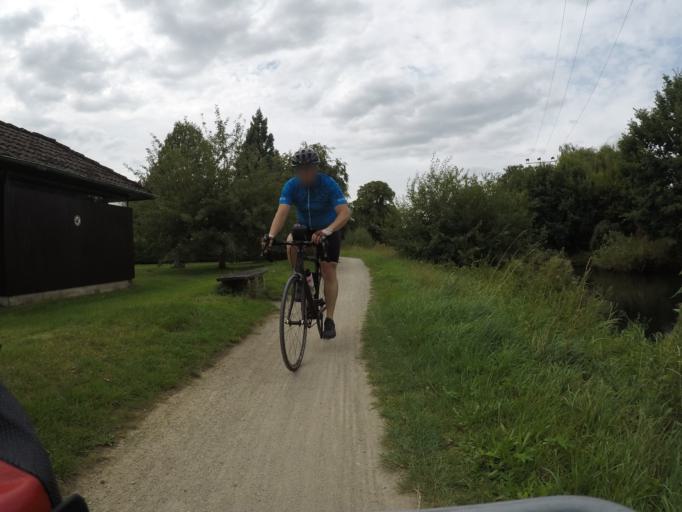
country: DE
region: Lower Saxony
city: Bardowick
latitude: 53.2992
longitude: 10.3980
